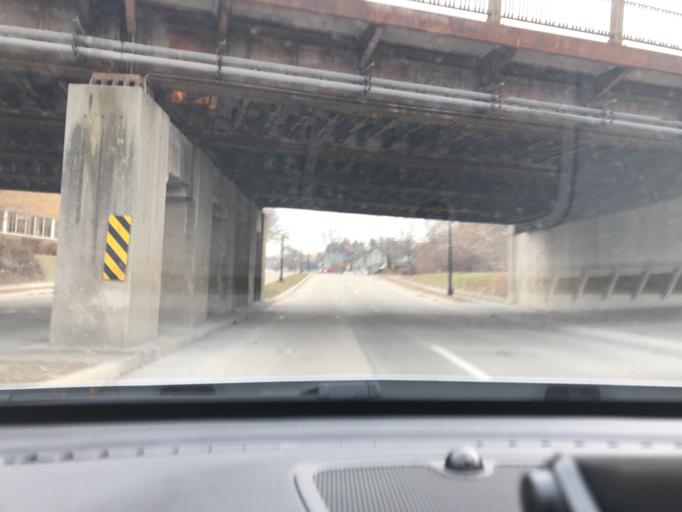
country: US
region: Michigan
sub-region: Wayne County
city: Dearborn Heights
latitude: 42.3033
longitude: -83.2509
